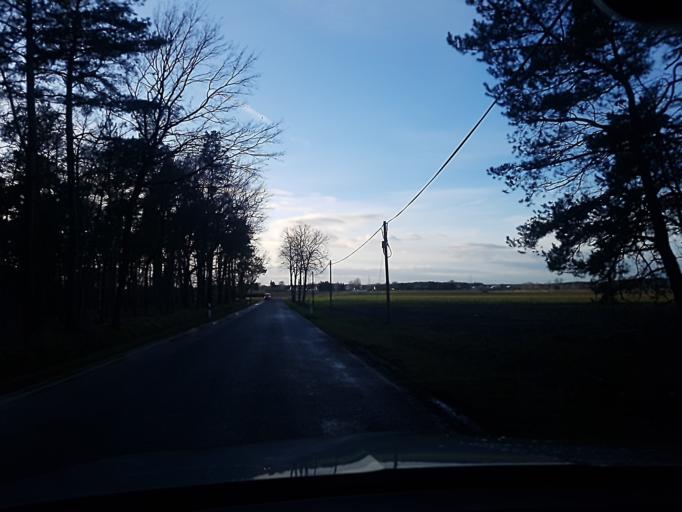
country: DE
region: Brandenburg
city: Schilda
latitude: 51.5881
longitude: 13.3983
